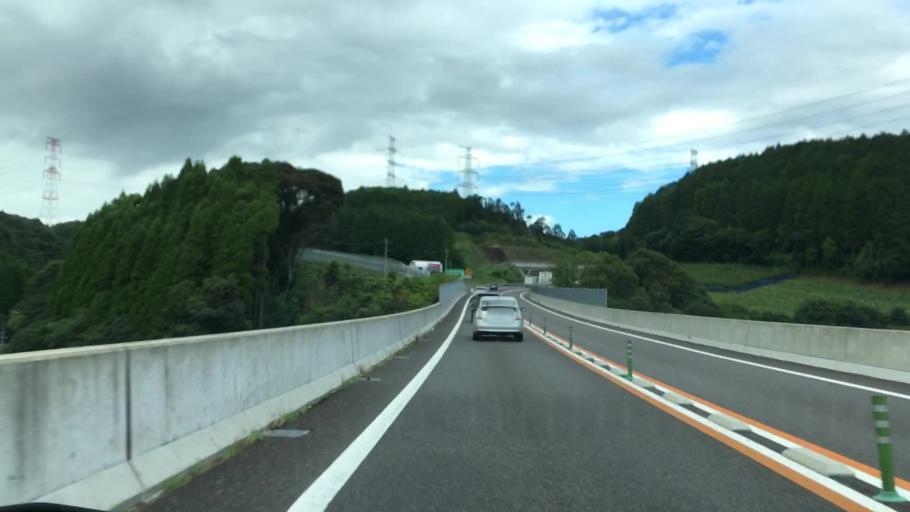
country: JP
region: Saga Prefecture
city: Imaricho-ko
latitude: 33.3486
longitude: 129.9246
